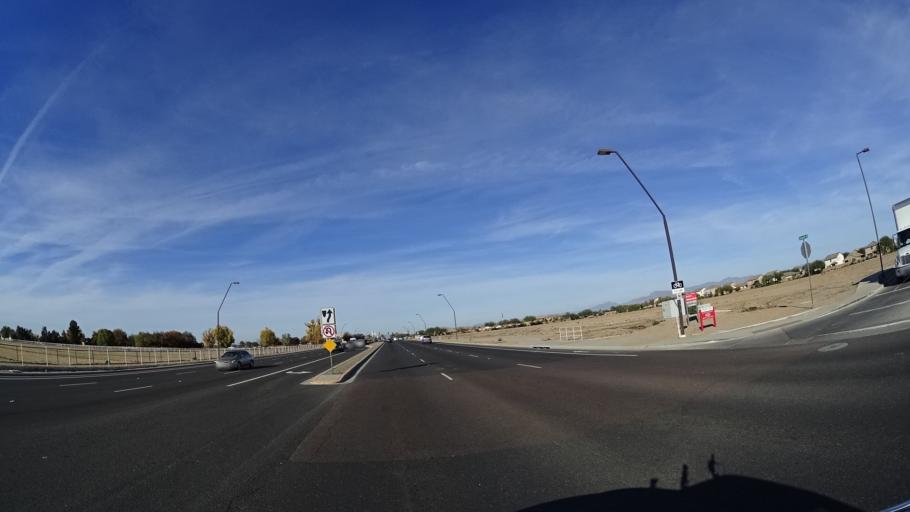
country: US
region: Arizona
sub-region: Maricopa County
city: Queen Creek
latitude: 33.2308
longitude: -111.6345
